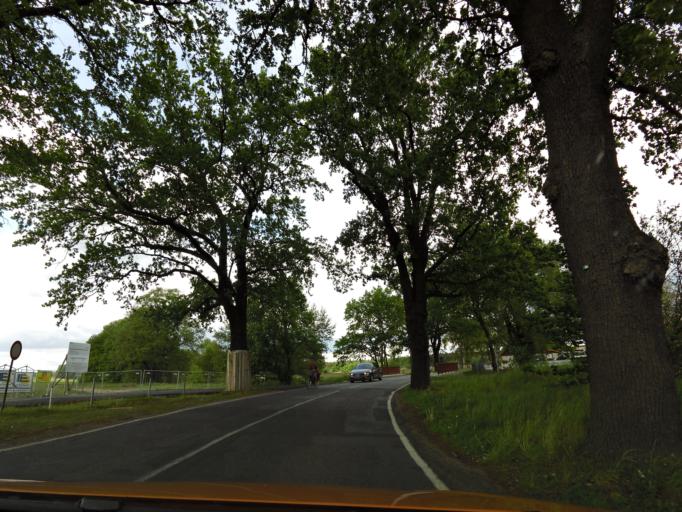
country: DE
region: Berlin
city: Wannsee
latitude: 52.3251
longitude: 13.1339
